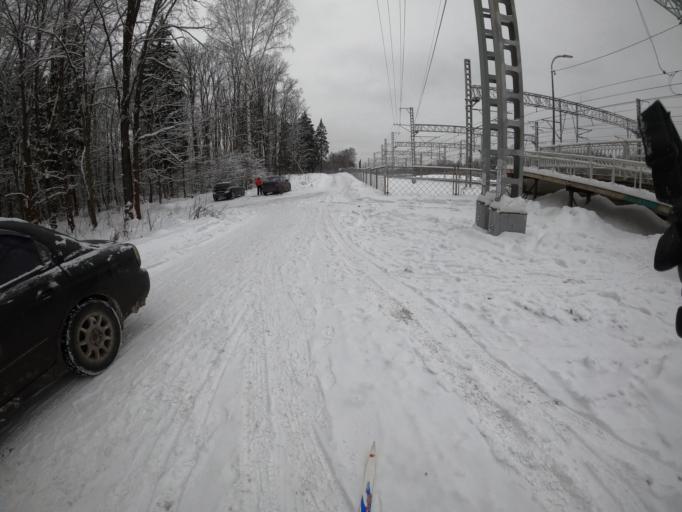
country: RU
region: Moscow
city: Zelenograd
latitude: 55.9692
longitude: 37.2101
